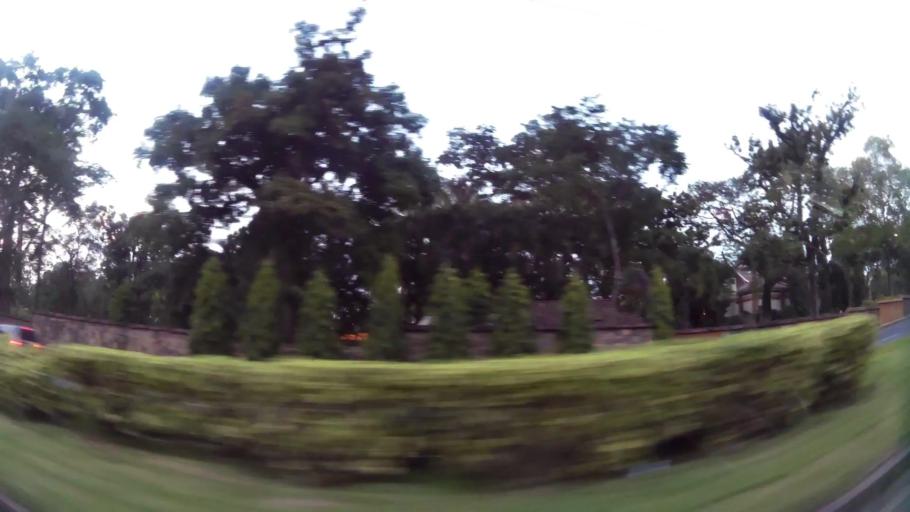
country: GT
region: Retalhuleu
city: Santa Cruz Mulua
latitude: 14.5968
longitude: -91.6145
